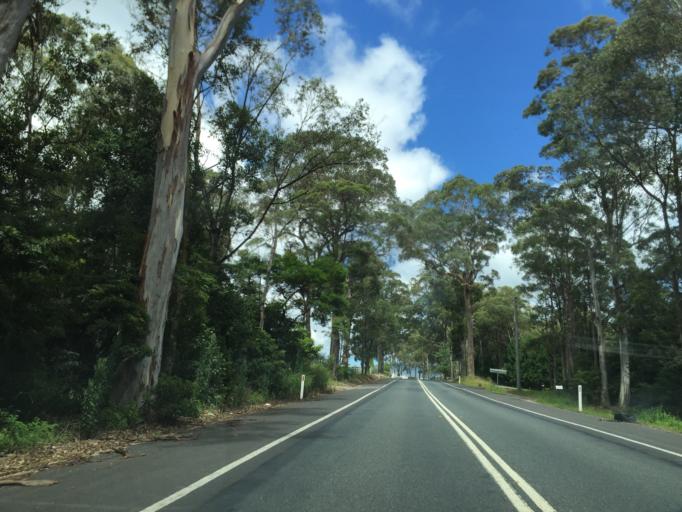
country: AU
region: New South Wales
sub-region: Hawkesbury
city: Richmond
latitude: -33.5027
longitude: 150.5370
